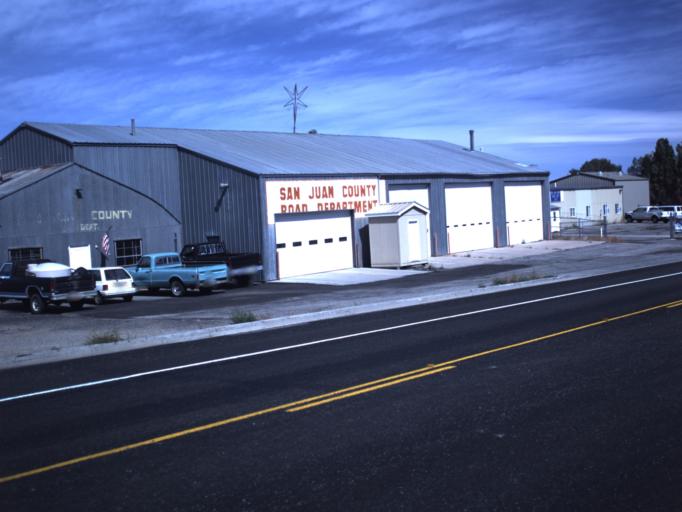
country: US
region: Utah
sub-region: San Juan County
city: Monticello
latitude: 37.8728
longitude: -109.3282
